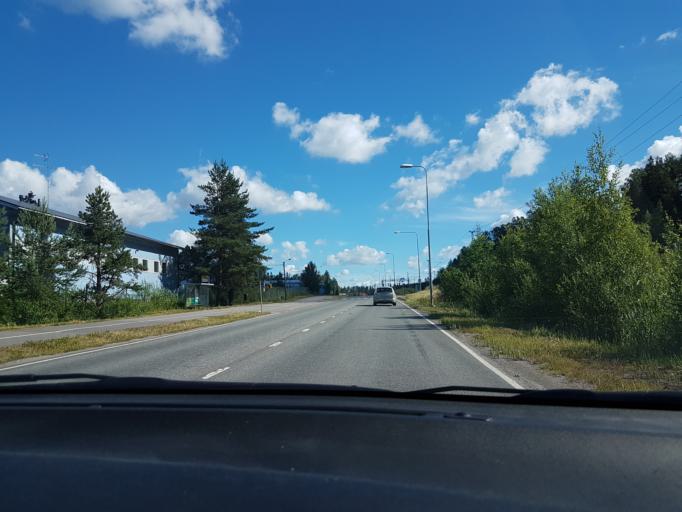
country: FI
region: Uusimaa
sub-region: Helsinki
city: Kerava
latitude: 60.3682
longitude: 25.0906
